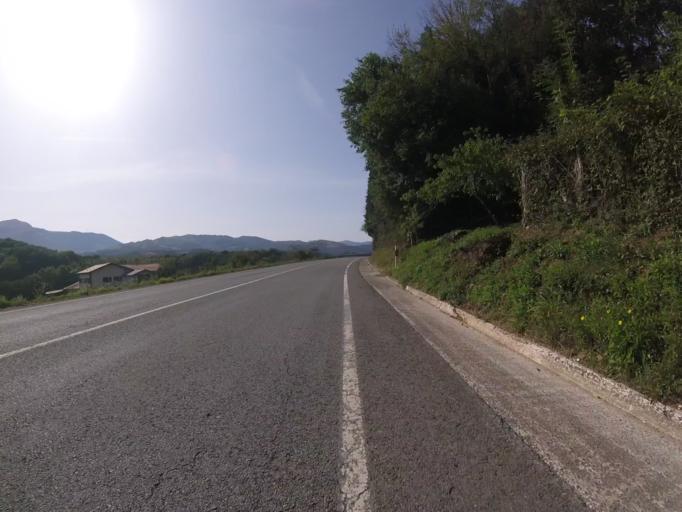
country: ES
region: Navarre
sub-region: Provincia de Navarra
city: Zugarramurdi
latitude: 43.1857
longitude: -1.4864
